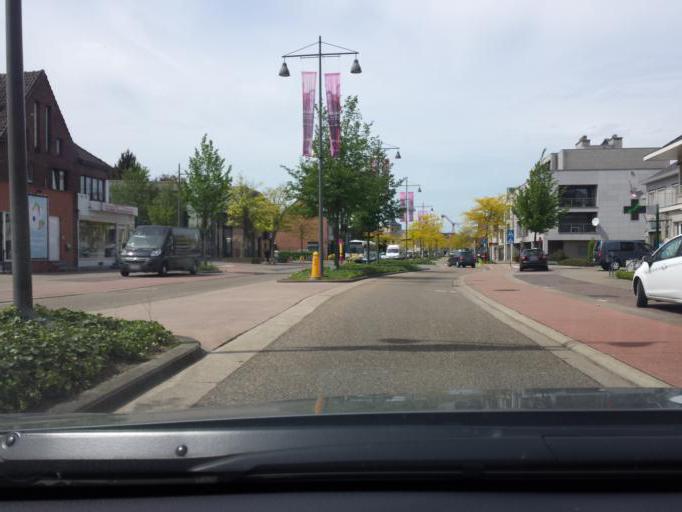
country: BE
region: Flanders
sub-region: Provincie Limburg
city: Lummen
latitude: 50.9461
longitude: 5.2576
